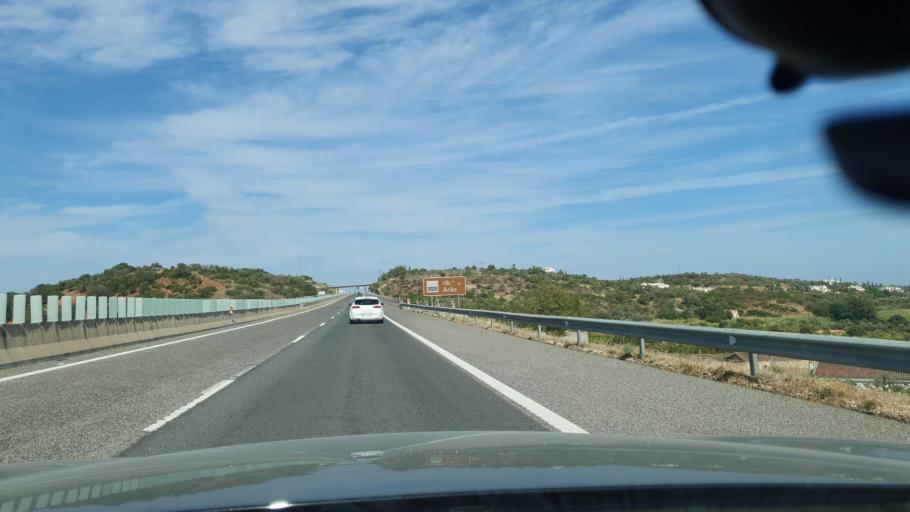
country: PT
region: Faro
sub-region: Portimao
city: Alvor
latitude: 37.1709
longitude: -8.6497
